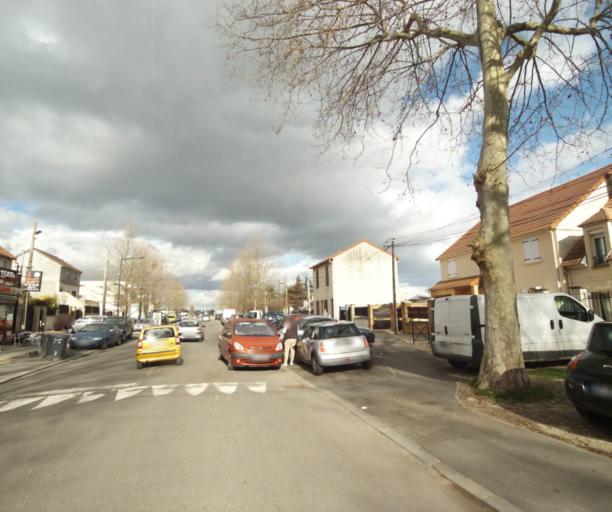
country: FR
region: Ile-de-France
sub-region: Departement de Seine-Saint-Denis
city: Pierrefitte-sur-Seine
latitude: 48.9726
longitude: 2.3650
